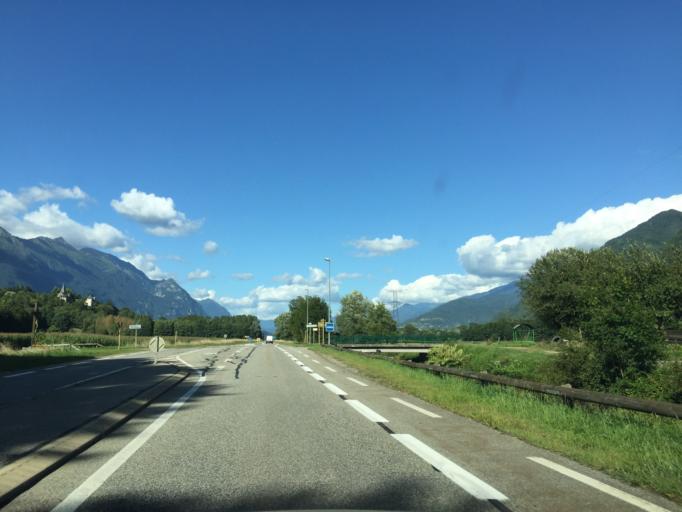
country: FR
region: Rhone-Alpes
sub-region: Departement de la Savoie
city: Coise-Saint-Jean-Pied-Gauthier
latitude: 45.5177
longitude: 6.1812
